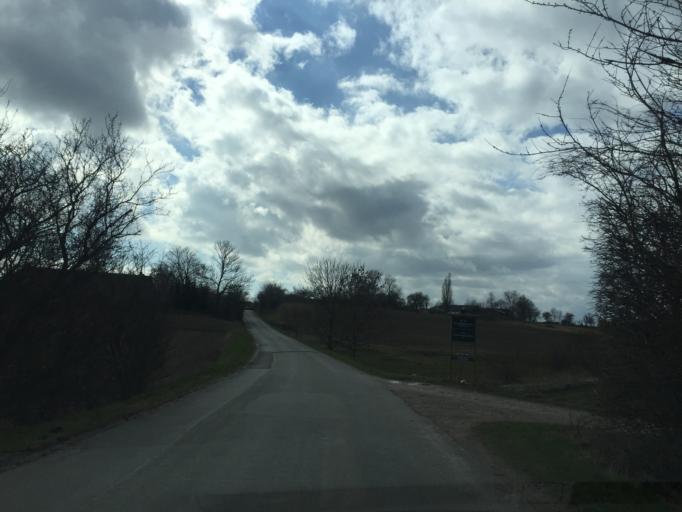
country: DK
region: South Denmark
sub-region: Svendborg Kommune
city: Svendborg
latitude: 55.0774
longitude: 10.4988
